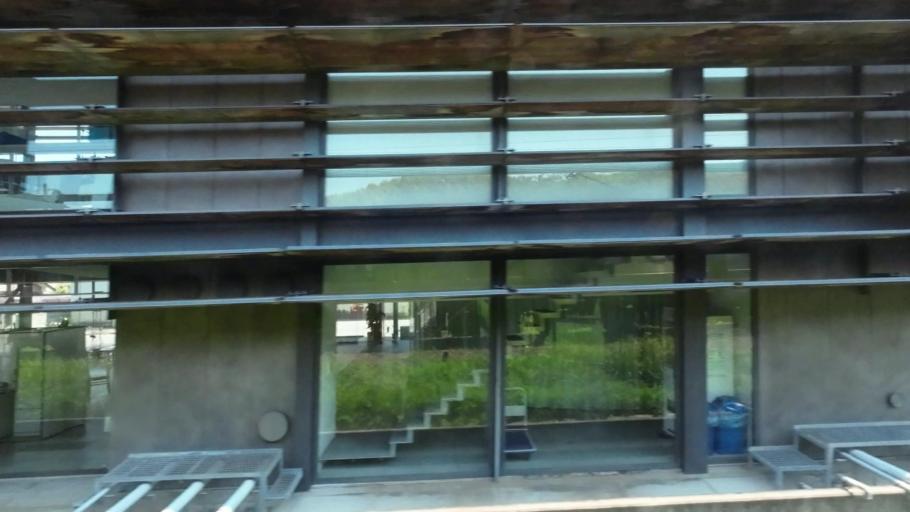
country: JP
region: Ehime
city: Hojo
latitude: 34.0962
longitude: 132.9719
